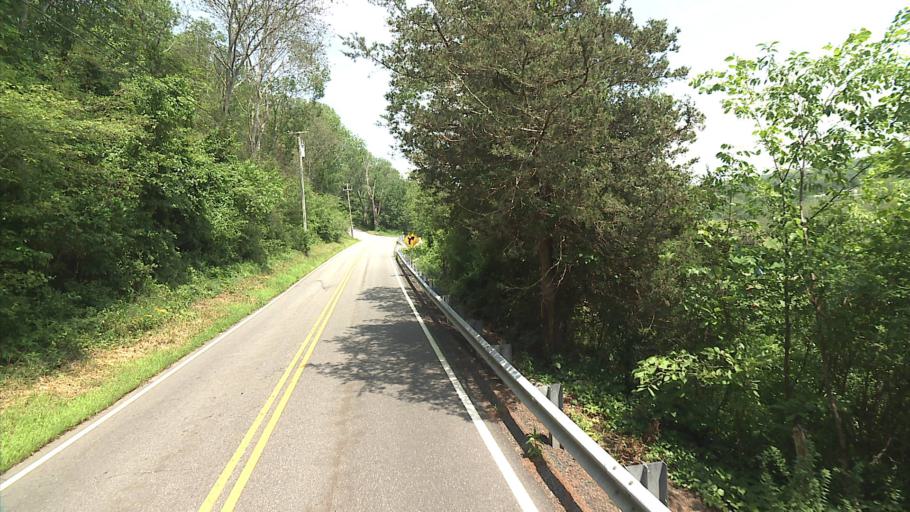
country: US
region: Connecticut
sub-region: Windham County
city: Moosup
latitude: 41.7555
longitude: -71.8532
